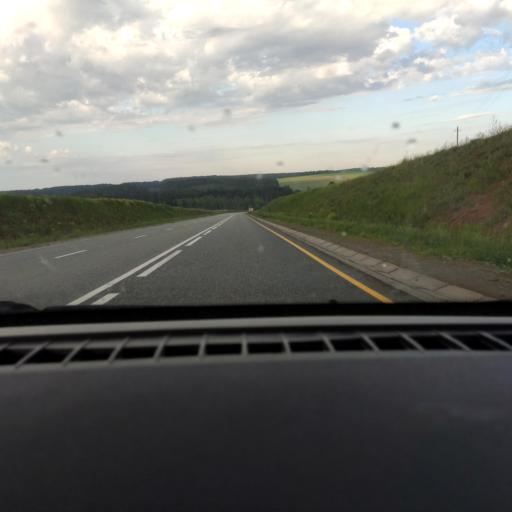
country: RU
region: Udmurtiya
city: Votkinsk
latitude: 57.2373
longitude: 54.1976
